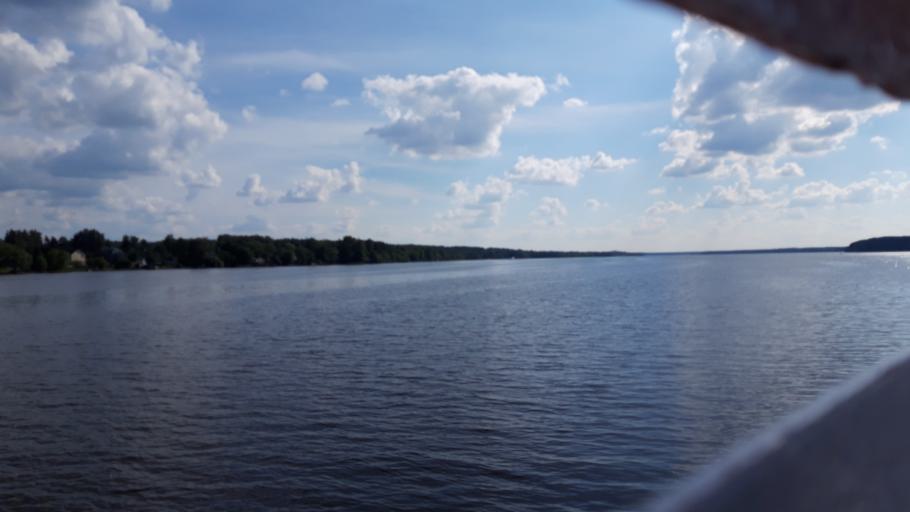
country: RU
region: Tverskaya
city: Konakovo
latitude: 56.6667
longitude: 36.6555
